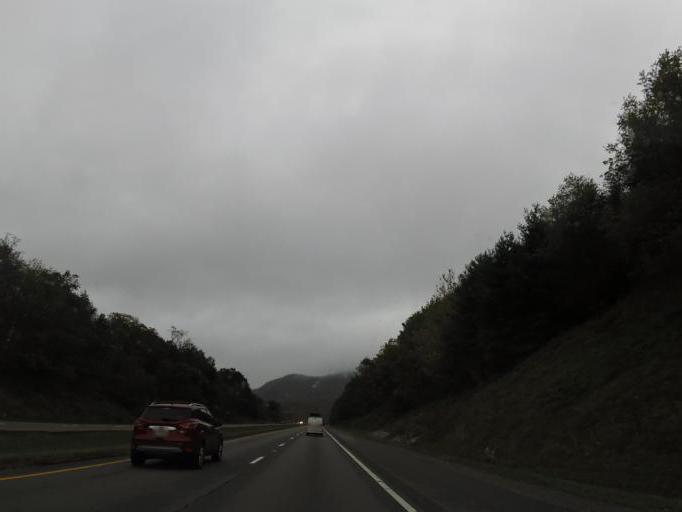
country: US
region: Virginia
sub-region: Wythe County
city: Wytheville
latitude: 37.0112
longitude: -81.1041
